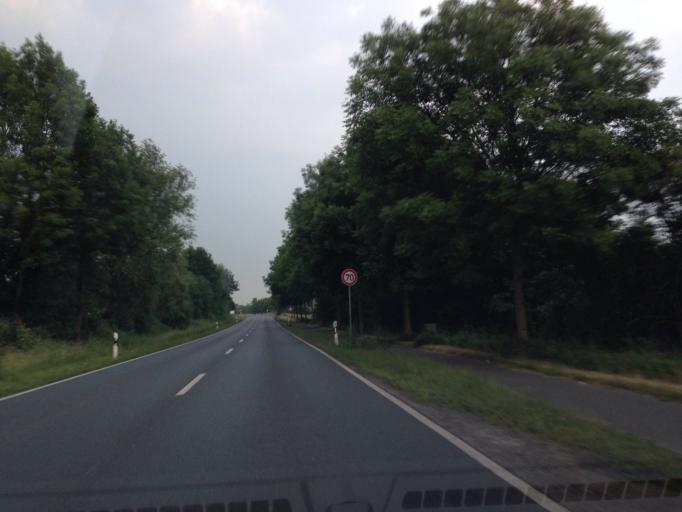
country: DE
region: North Rhine-Westphalia
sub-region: Regierungsbezirk Munster
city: Nottuln
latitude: 51.9251
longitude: 7.3661
